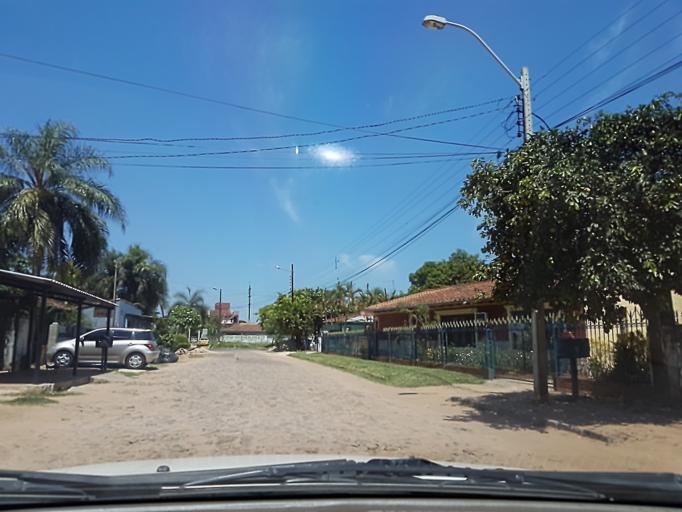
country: PY
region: Central
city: Fernando de la Mora
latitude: -25.2941
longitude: -57.5373
